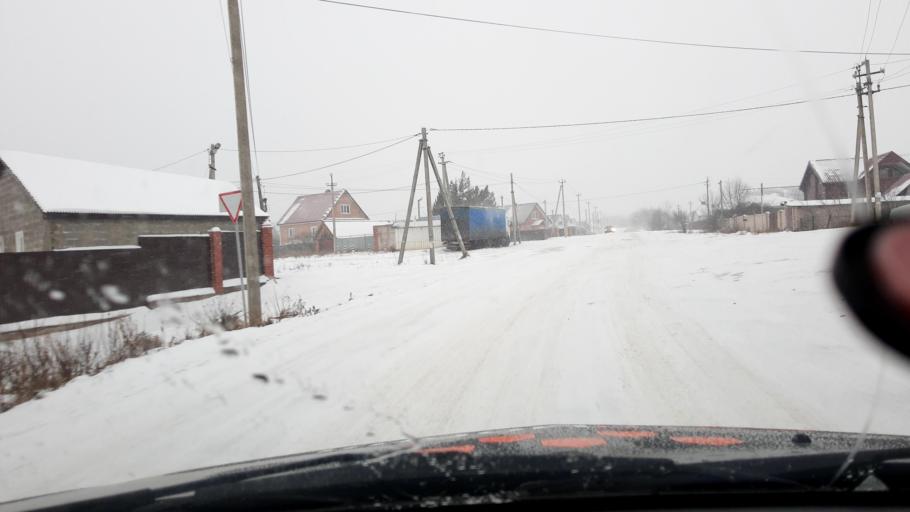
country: RU
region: Bashkortostan
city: Ufa
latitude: 54.5434
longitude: 55.9404
